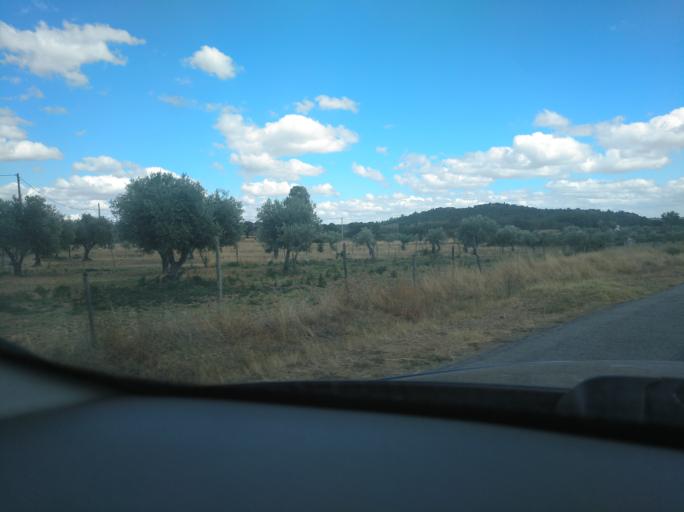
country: ES
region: Extremadura
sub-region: Provincia de Badajoz
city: La Codosera
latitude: 39.1524
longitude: -7.1606
